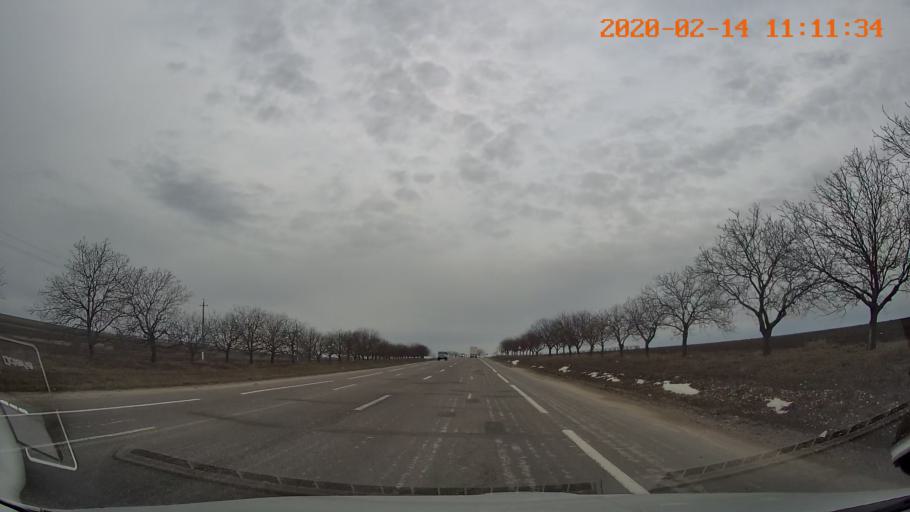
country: MD
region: Raionul Edinet
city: Edinet
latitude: 48.1986
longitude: 27.2743
